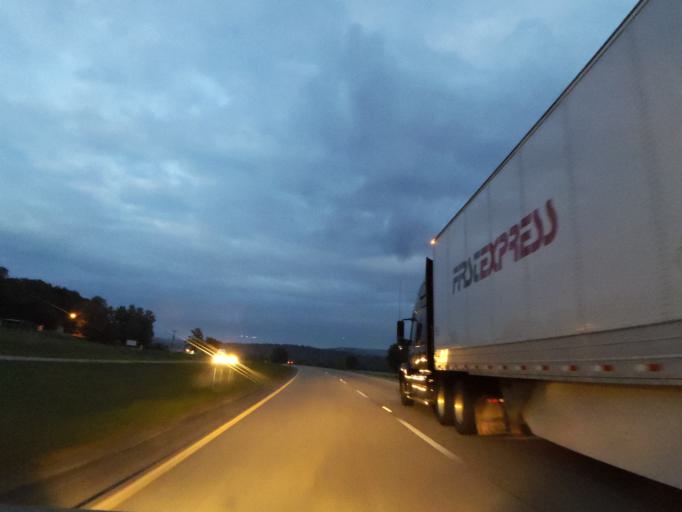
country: US
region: Alabama
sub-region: Madison County
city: New Hope
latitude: 34.6063
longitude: -86.2567
